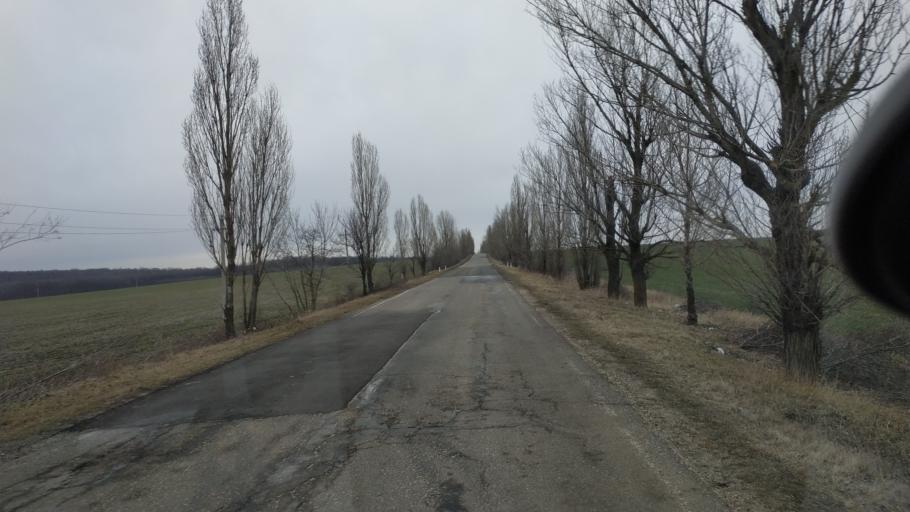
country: MD
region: Telenesti
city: Cocieri
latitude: 47.3724
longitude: 29.0430
